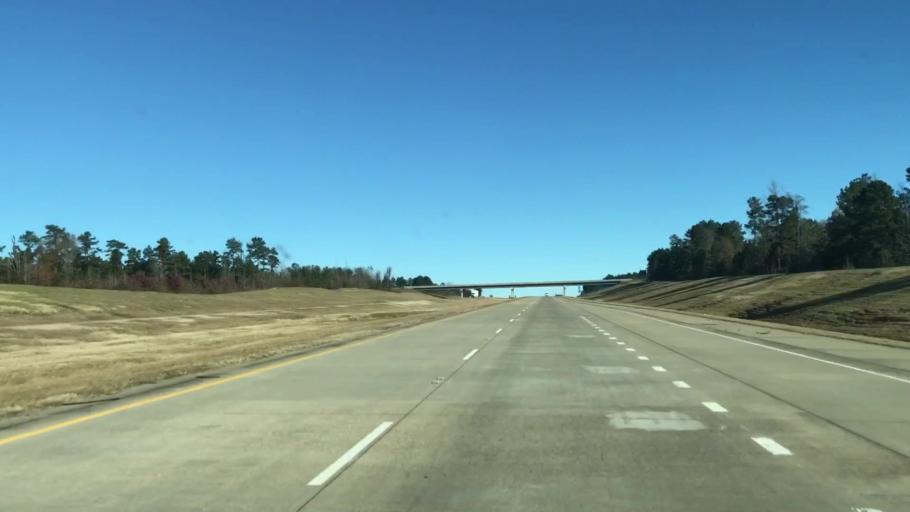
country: US
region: Louisiana
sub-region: Caddo Parish
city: Vivian
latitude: 33.0037
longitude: -93.9068
